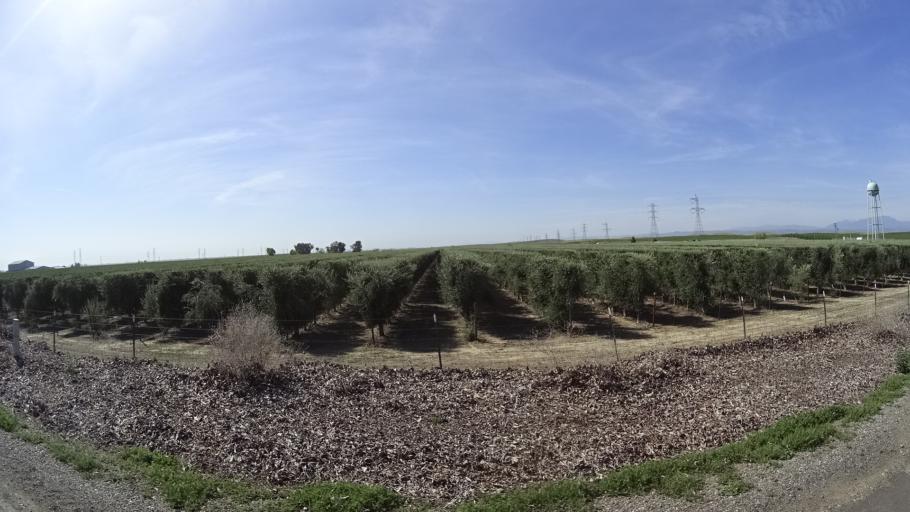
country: US
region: California
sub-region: Glenn County
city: Willows
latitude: 39.6116
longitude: -122.2716
